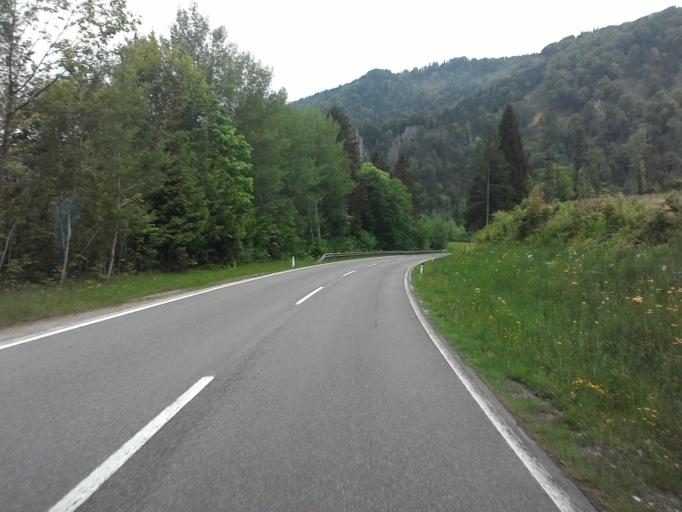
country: AT
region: Styria
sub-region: Politischer Bezirk Liezen
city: Altenmarkt bei Sankt Gallen
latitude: 47.7678
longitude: 14.6493
